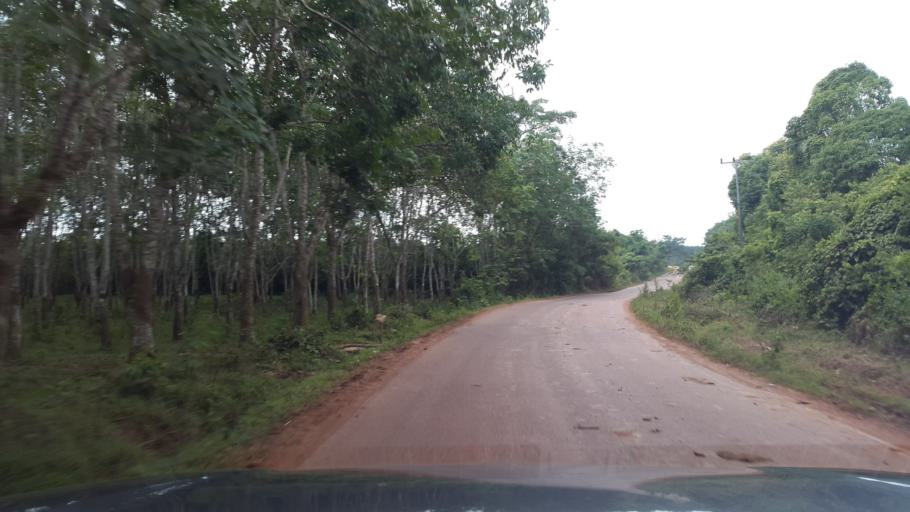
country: ID
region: South Sumatra
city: Sungaigerong
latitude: -3.1633
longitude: 104.8926
